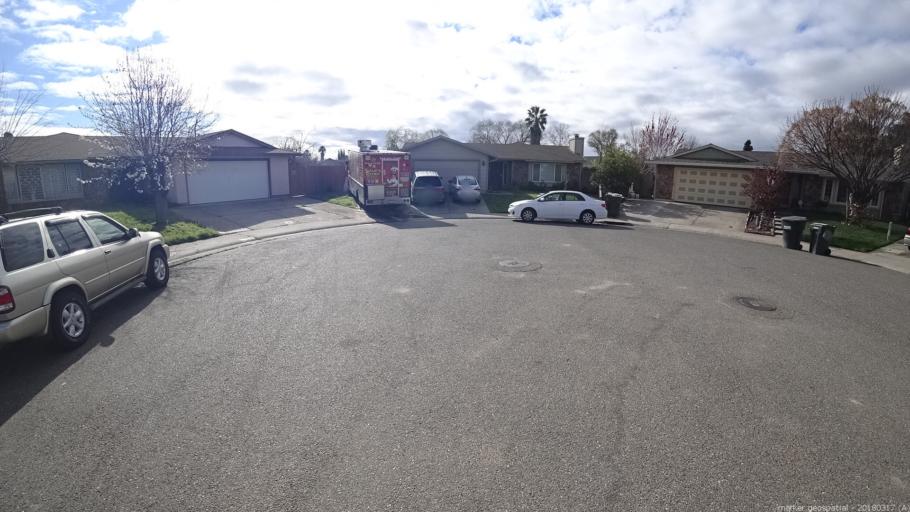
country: US
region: California
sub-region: Sacramento County
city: Florin
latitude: 38.4733
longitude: -121.4021
